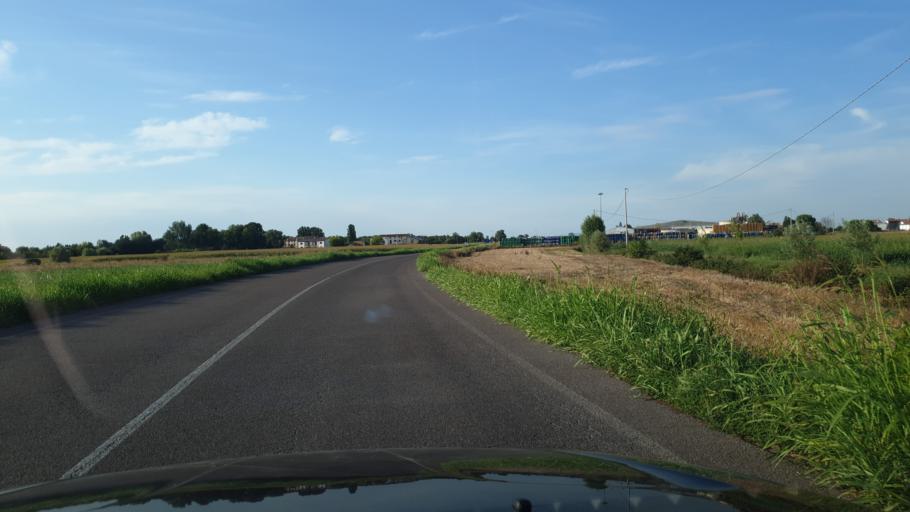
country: IT
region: Veneto
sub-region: Provincia di Rovigo
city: Fiesso Umbertiano
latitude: 44.9557
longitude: 11.6157
